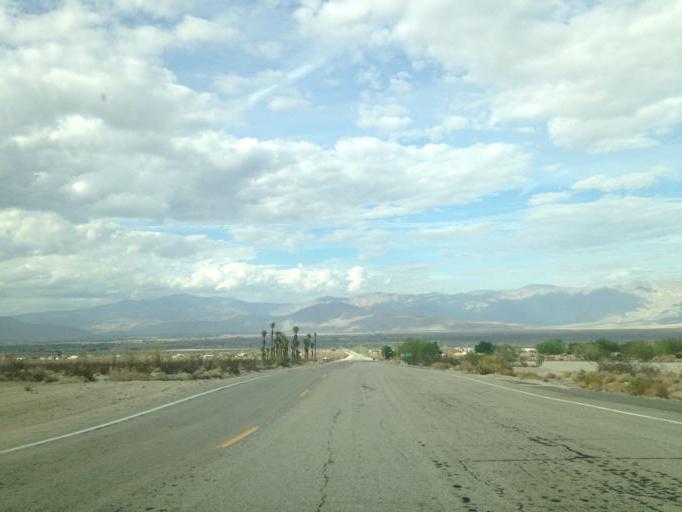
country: US
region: California
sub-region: San Diego County
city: Borrego Springs
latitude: 33.1930
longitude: -116.3305
